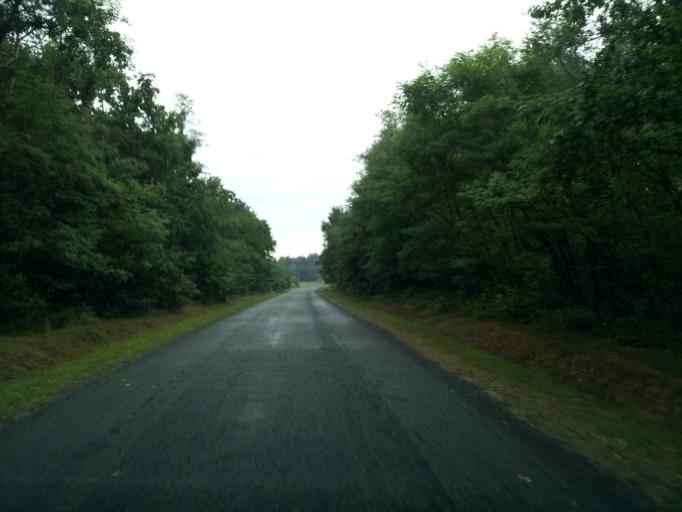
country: HU
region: Zala
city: Zalalovo
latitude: 46.8825
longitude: 16.5475
